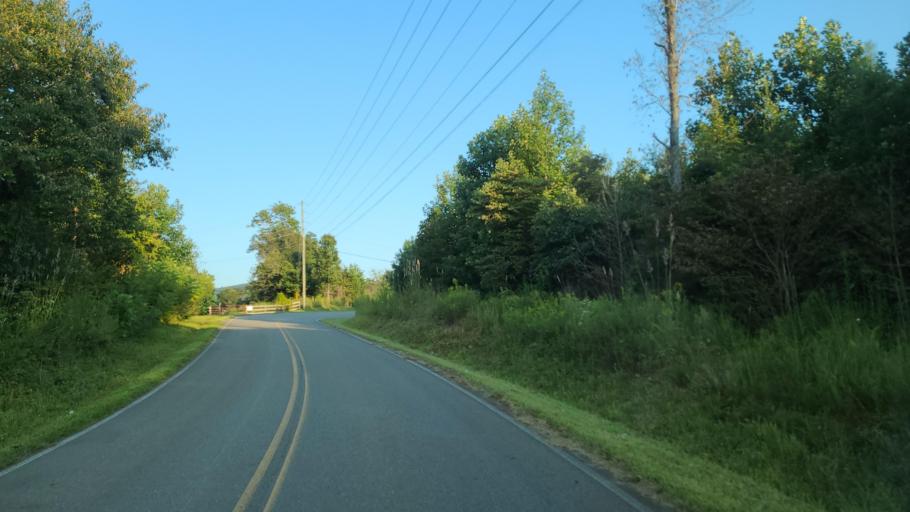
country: US
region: Georgia
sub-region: Pickens County
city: Jasper
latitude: 34.4444
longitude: -84.5492
